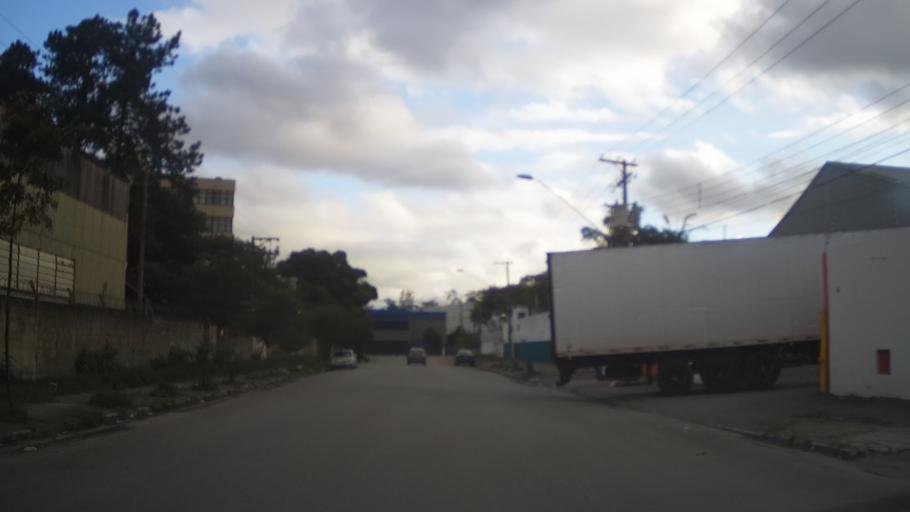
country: BR
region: Sao Paulo
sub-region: Guarulhos
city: Guarulhos
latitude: -23.4776
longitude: -46.4638
